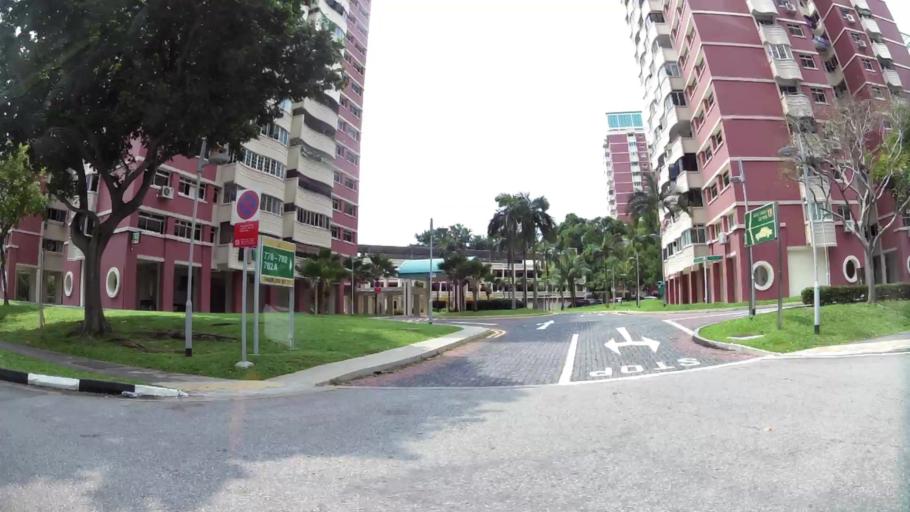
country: MY
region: Johor
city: Kampung Pasir Gudang Baru
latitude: 1.3738
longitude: 103.9390
